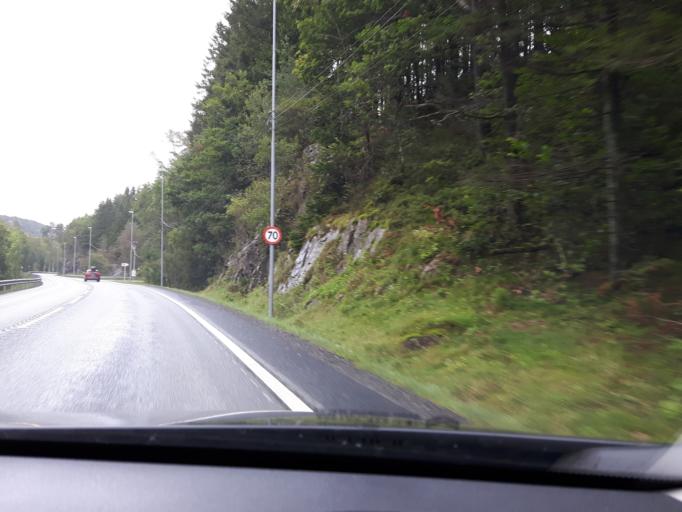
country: NO
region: Vest-Agder
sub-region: Marnardal
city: Helland
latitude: 58.0850
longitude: 7.6192
